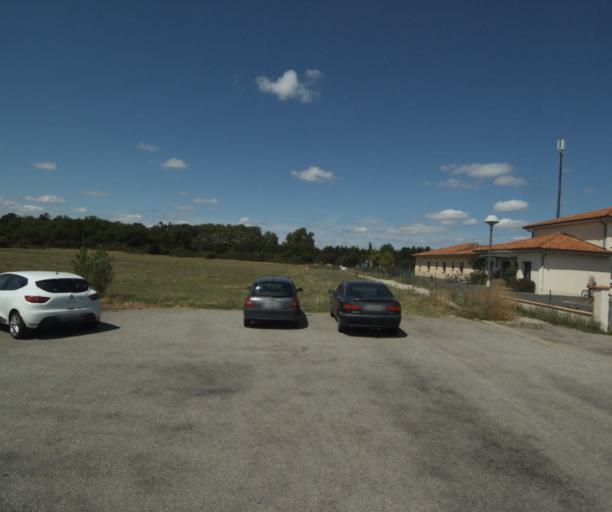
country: FR
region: Midi-Pyrenees
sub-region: Departement de la Haute-Garonne
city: Revel
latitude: 43.4631
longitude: 2.0172
